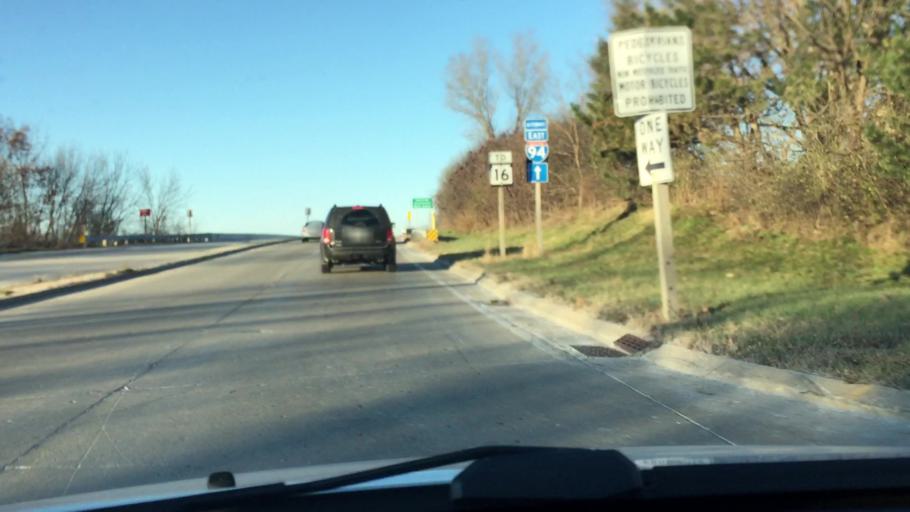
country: US
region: Wisconsin
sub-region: Waukesha County
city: Oconomowoc
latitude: 43.1045
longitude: -88.4805
